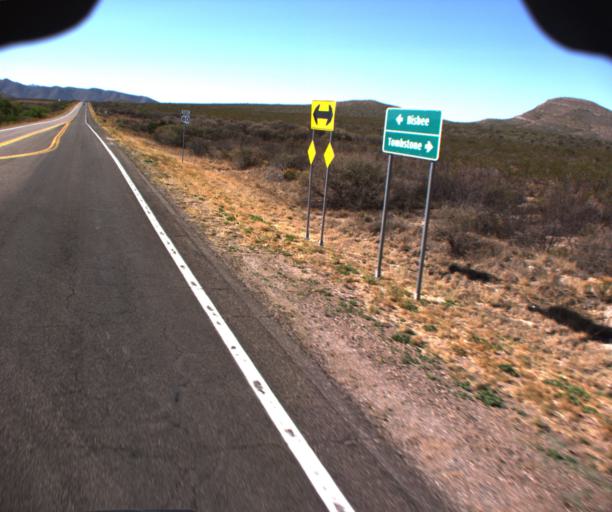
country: US
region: Arizona
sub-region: Cochise County
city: Tombstone
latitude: 31.6731
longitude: -110.0322
